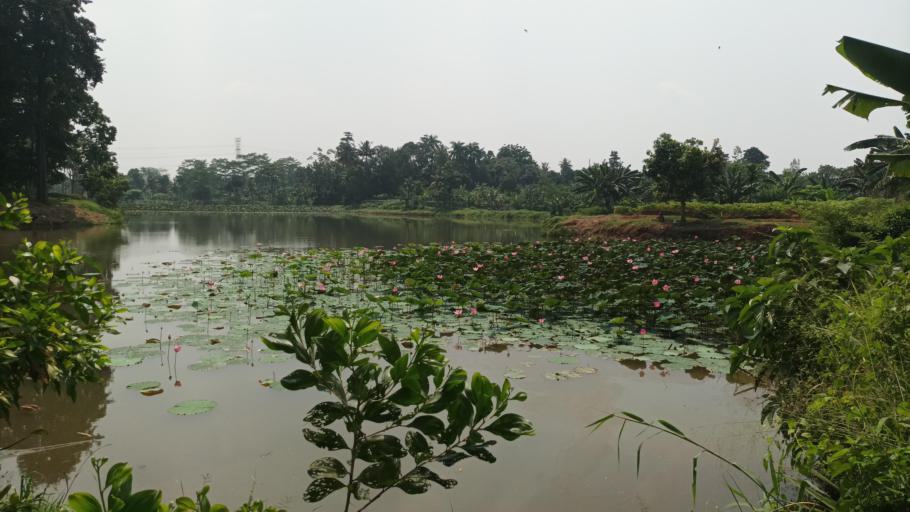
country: ID
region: West Java
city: Depok
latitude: -6.4253
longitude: 106.8589
